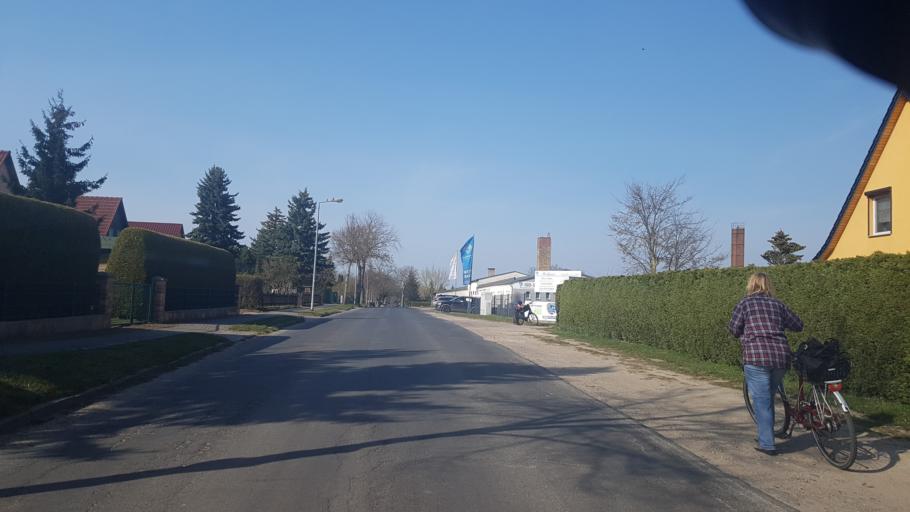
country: DE
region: Brandenburg
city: Prenzlau
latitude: 53.2241
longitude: 13.8432
